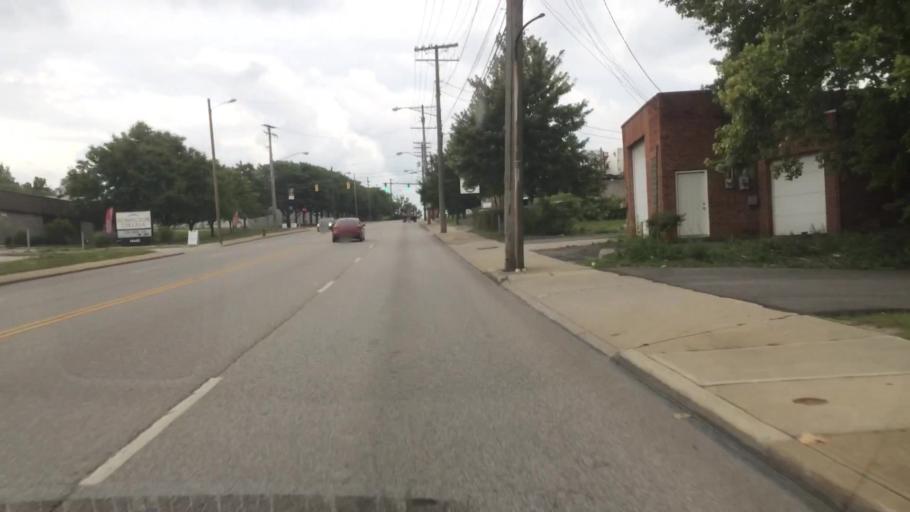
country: US
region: Ohio
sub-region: Cuyahoga County
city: Maple Heights
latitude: 41.4241
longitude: -81.5823
